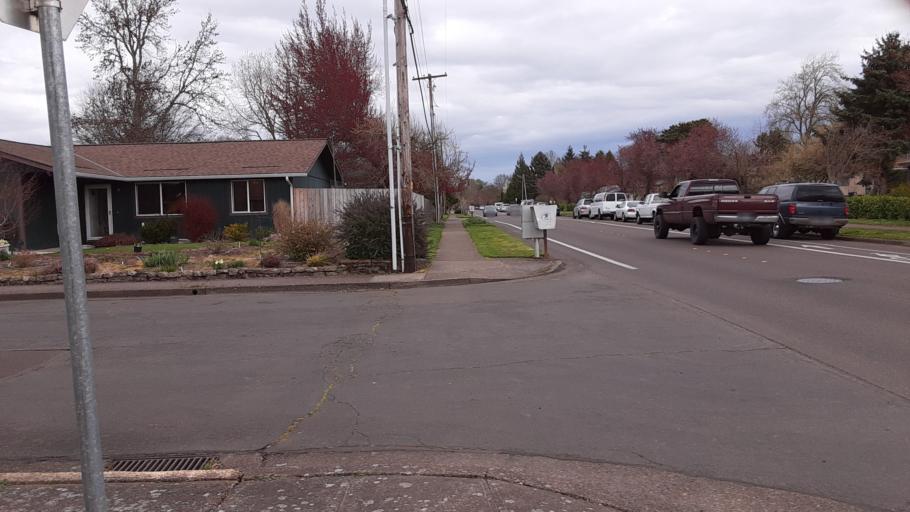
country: US
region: Oregon
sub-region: Benton County
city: Corvallis
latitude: 44.5368
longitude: -123.2641
